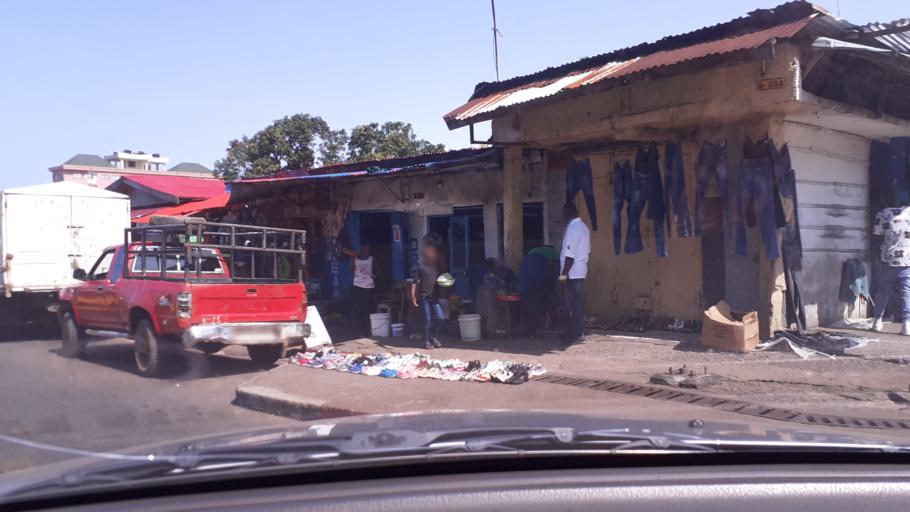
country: LR
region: Montserrado
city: Monrovia
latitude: 6.3135
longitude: -10.8014
